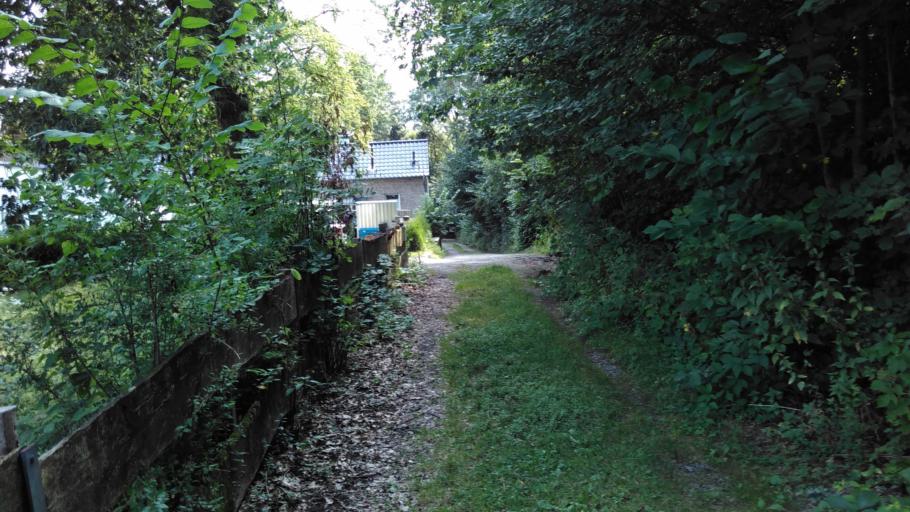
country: DE
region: North Rhine-Westphalia
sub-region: Regierungsbezirk Detmold
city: Lage
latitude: 52.0020
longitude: 8.7936
